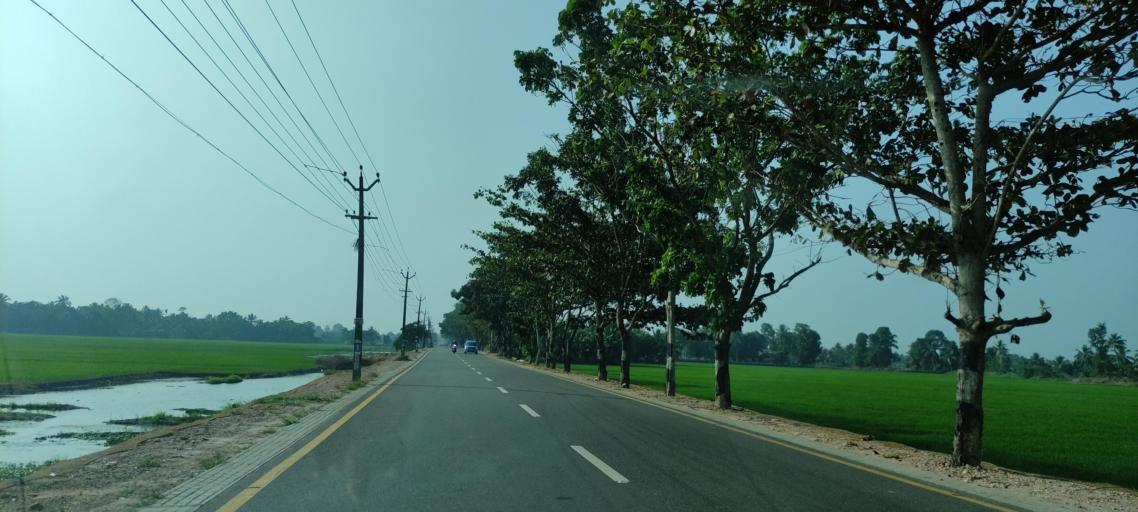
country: IN
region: Kerala
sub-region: Kottayam
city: Changanacheri
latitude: 9.3652
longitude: 76.4401
